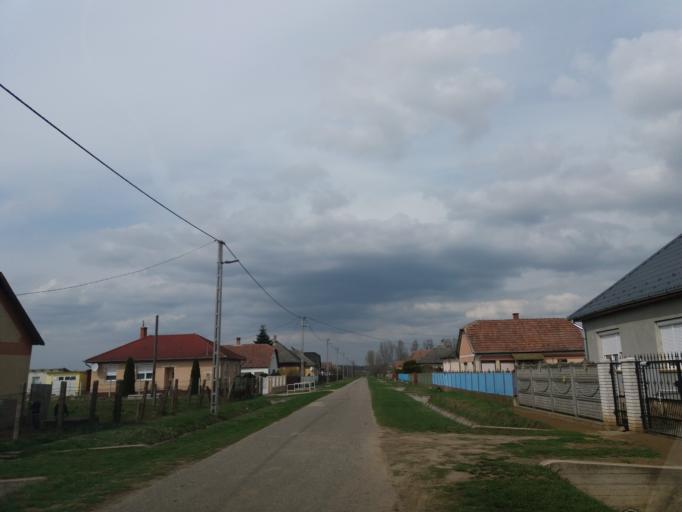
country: HU
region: Szabolcs-Szatmar-Bereg
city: Petnehaza
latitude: 48.0521
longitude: 22.0374
